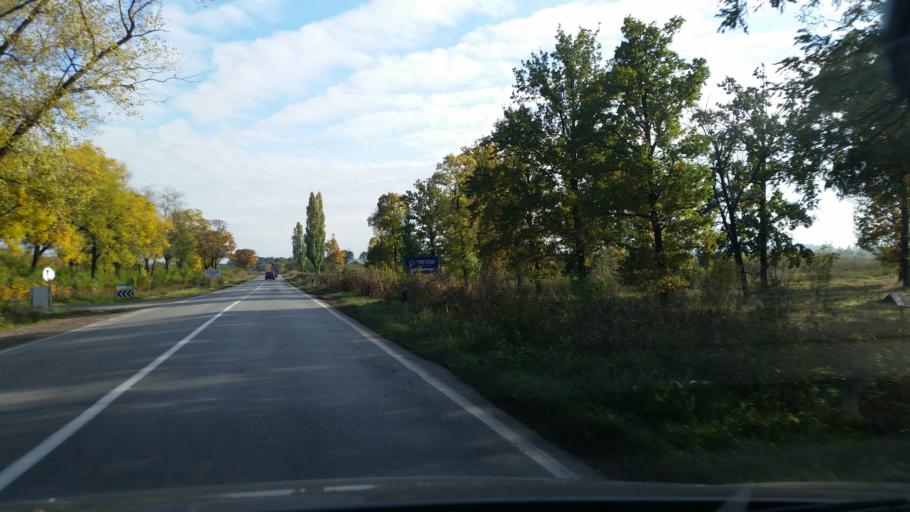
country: RS
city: Ecka
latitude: 45.3365
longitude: 20.4343
